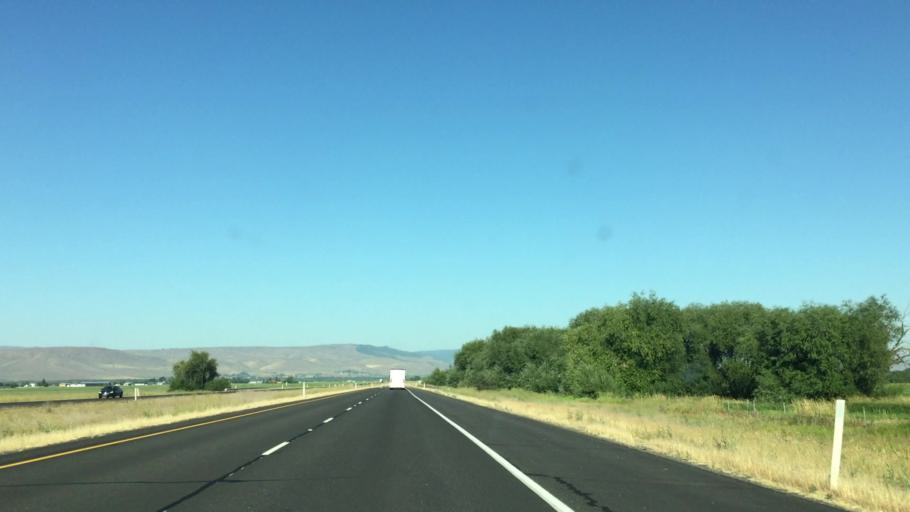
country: US
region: Washington
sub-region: Kittitas County
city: Kittitas
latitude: 46.9697
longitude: -120.4413
